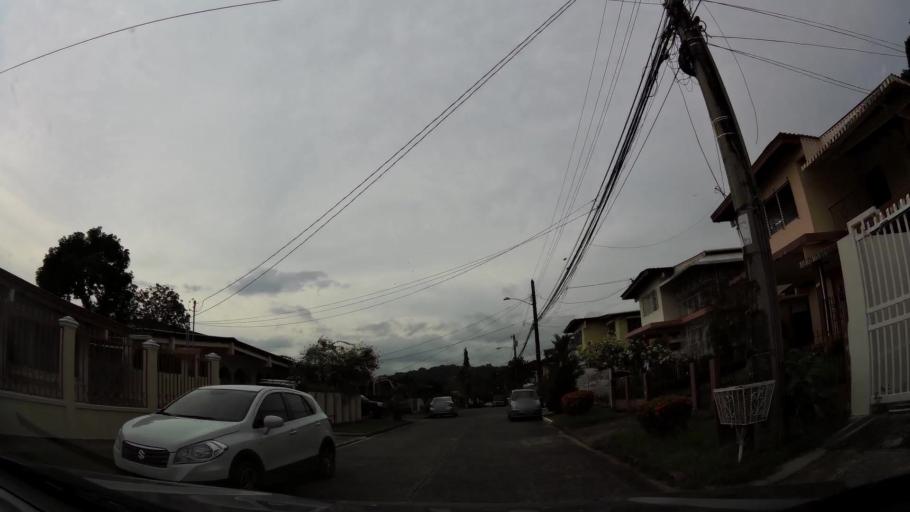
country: PA
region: Panama
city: Panama
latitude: 9.0113
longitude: -79.5392
